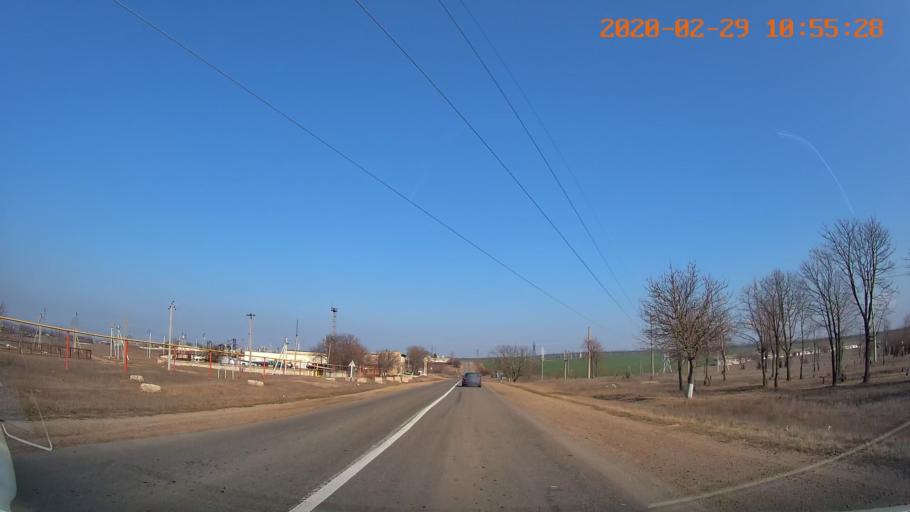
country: MD
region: Telenesti
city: Grigoriopol
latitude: 47.1342
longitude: 29.3251
